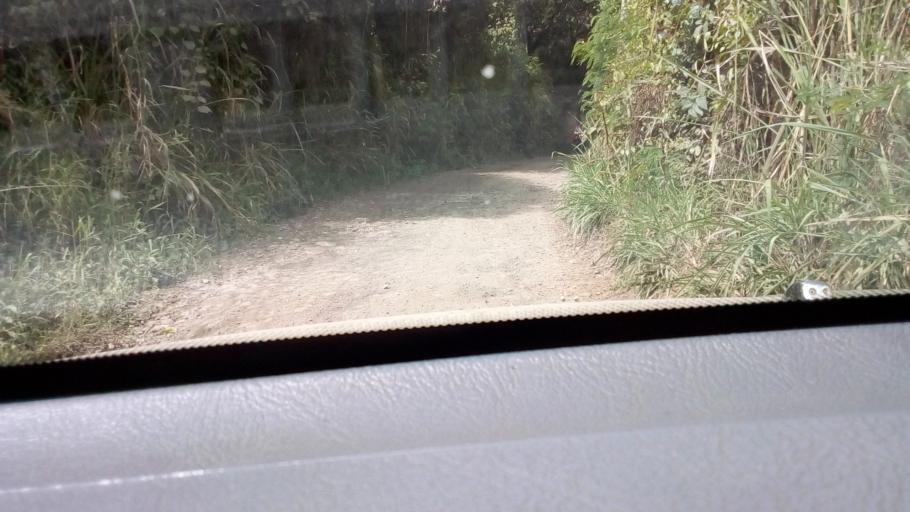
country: CO
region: Cundinamarca
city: Tenza
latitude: 5.0800
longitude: -73.4186
